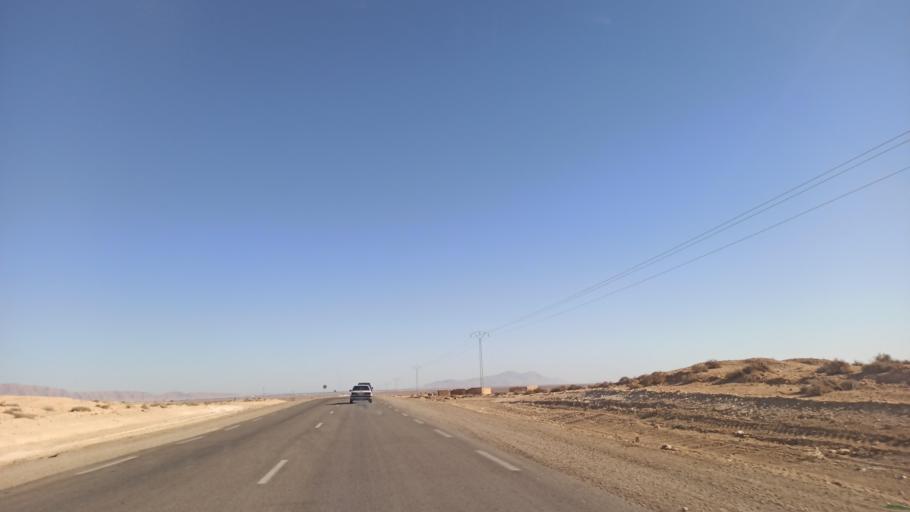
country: TN
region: Gafsa
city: Al Metlaoui
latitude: 34.3302
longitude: 8.5521
